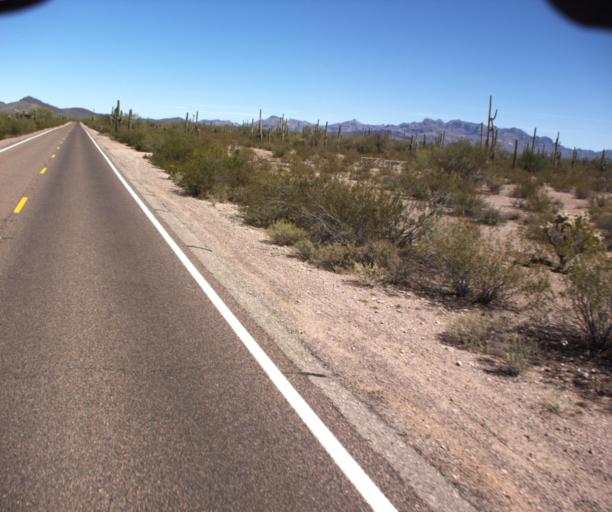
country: MX
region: Sonora
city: Sonoyta
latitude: 31.8996
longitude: -112.8115
